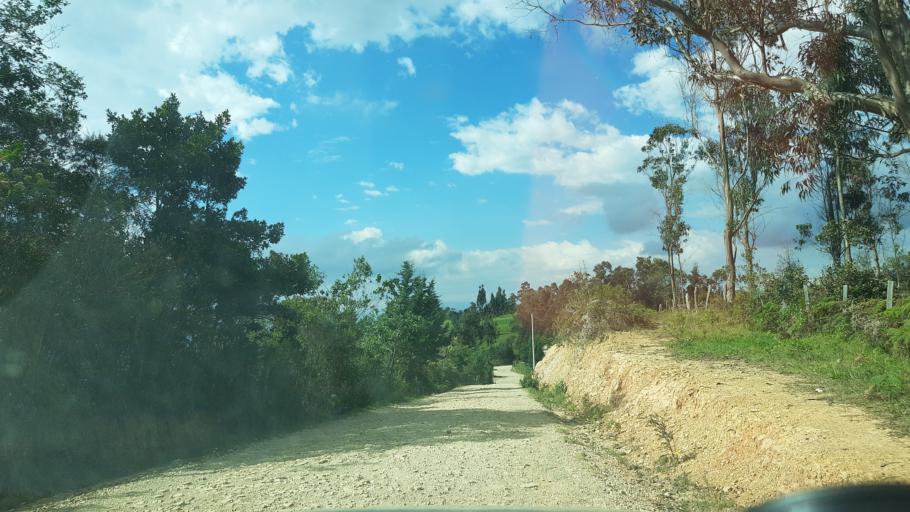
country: CO
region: Boyaca
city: Santa Sofia
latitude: 5.7379
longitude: -73.5516
